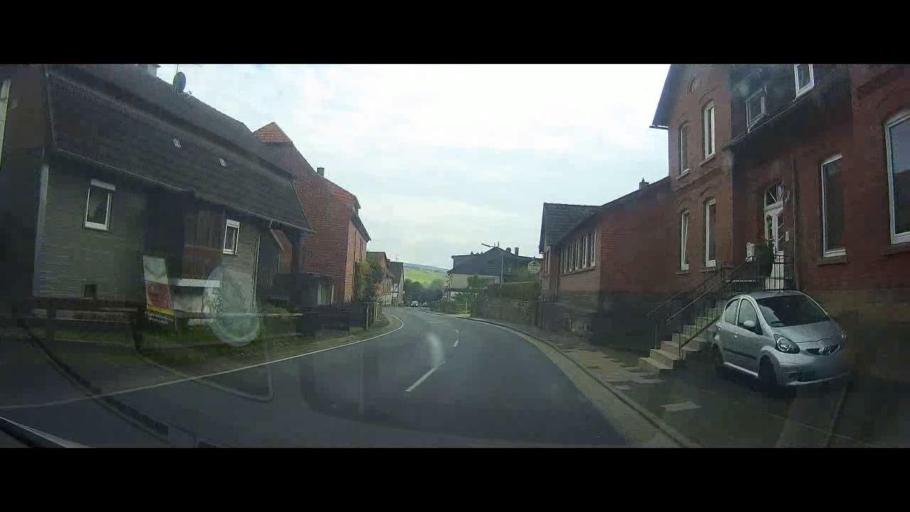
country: DE
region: Lower Saxony
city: Uslar
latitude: 51.6519
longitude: 9.6502
